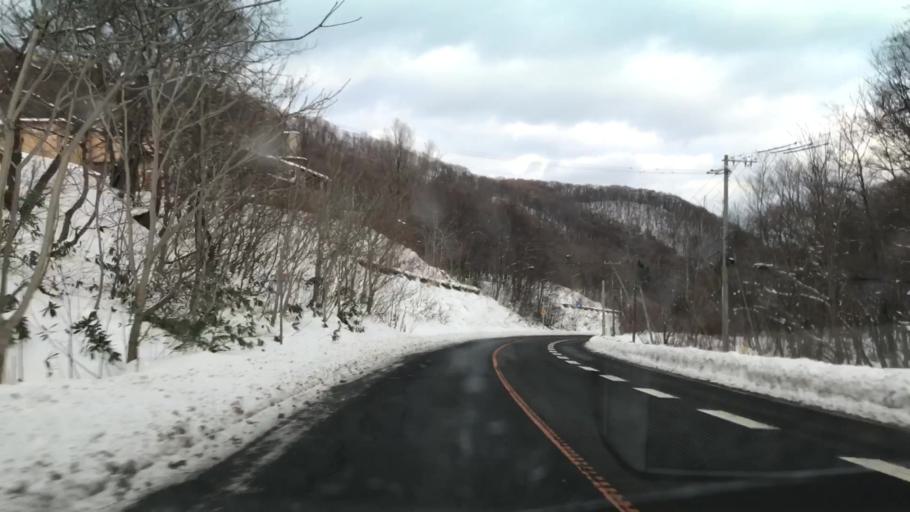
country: JP
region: Hokkaido
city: Yoichi
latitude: 43.2238
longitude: 140.7350
